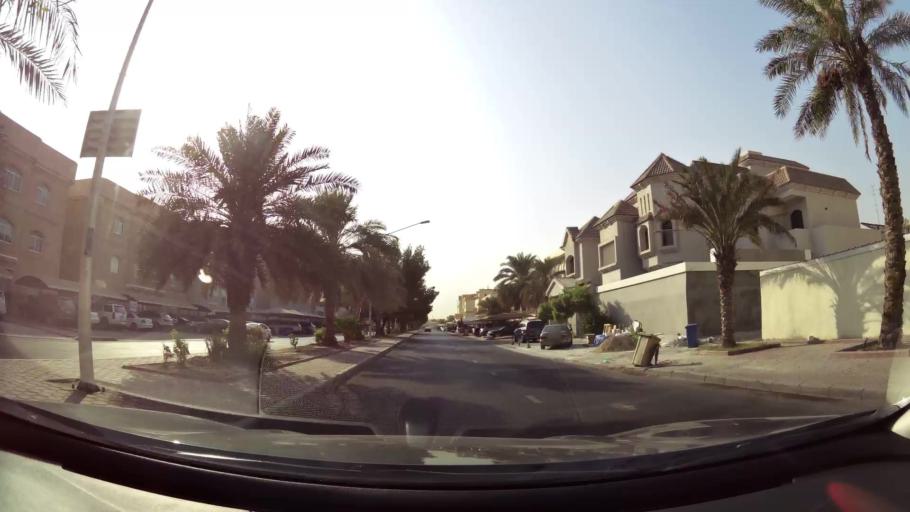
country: KW
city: Bayan
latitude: 29.3142
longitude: 48.0398
